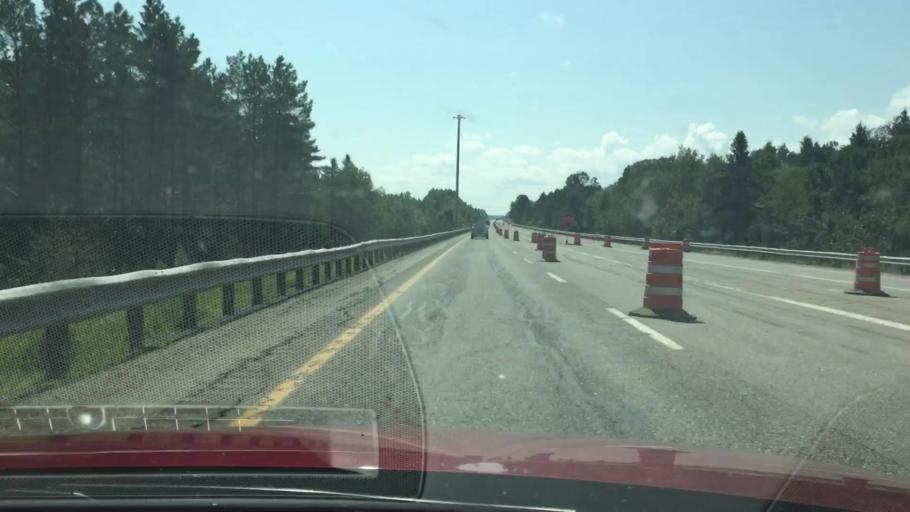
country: US
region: Maine
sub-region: Penobscot County
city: Patten
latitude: 45.8706
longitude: -68.4147
